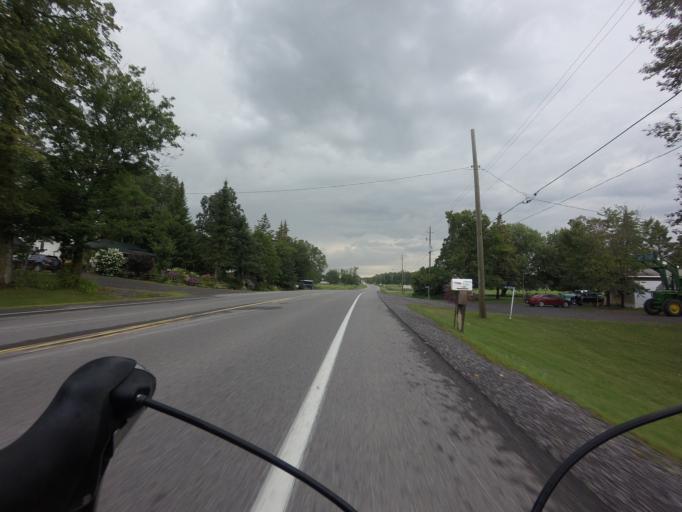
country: CA
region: Ontario
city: Carleton Place
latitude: 45.1458
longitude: -75.9682
